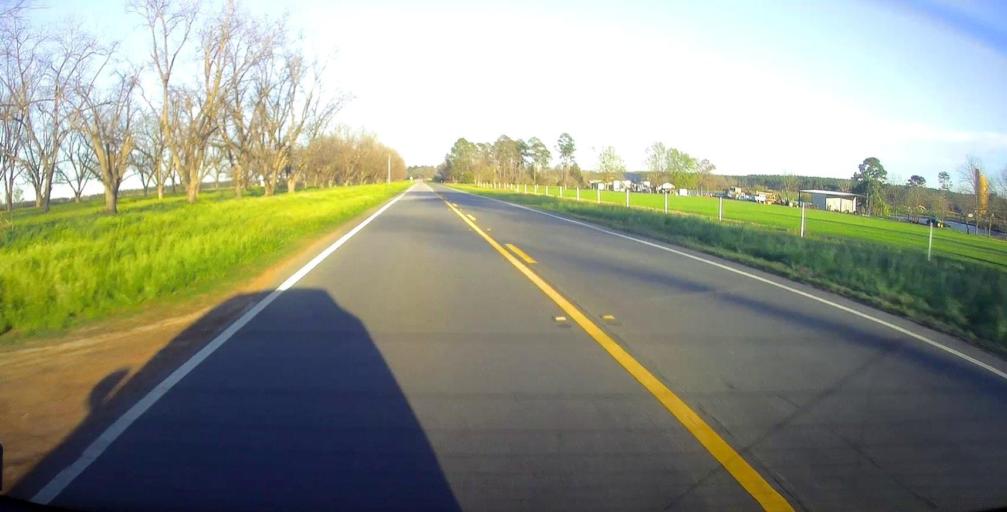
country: US
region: Georgia
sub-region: Wilcox County
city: Rochelle
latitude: 31.9609
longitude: -83.4114
